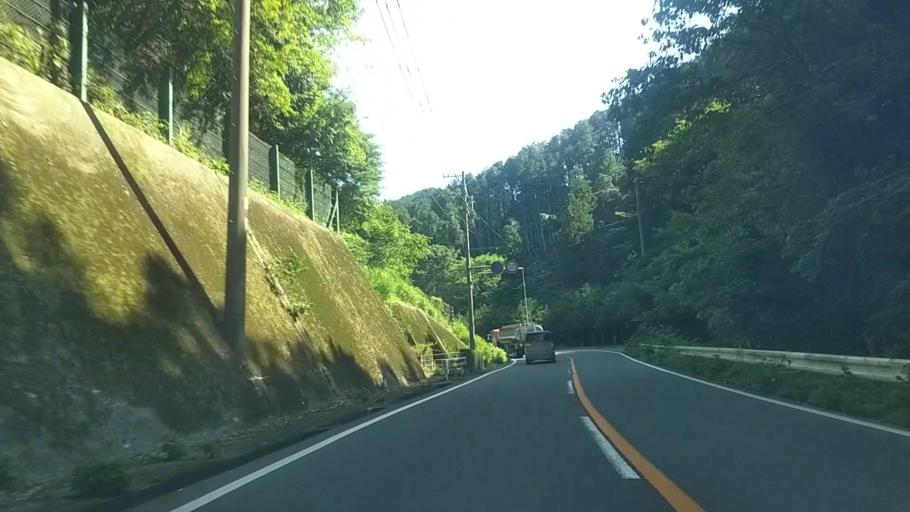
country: JP
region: Shizuoka
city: Fujinomiya
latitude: 35.1739
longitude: 138.5229
